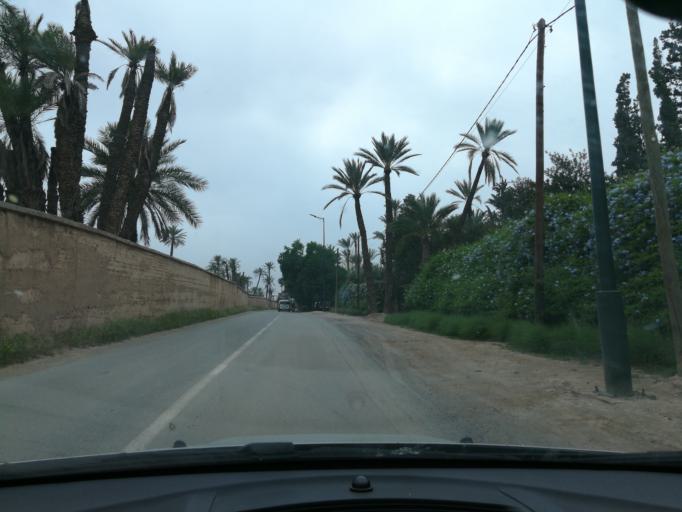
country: MA
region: Marrakech-Tensift-Al Haouz
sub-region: Marrakech
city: Marrakesh
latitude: 31.6655
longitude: -7.9664
